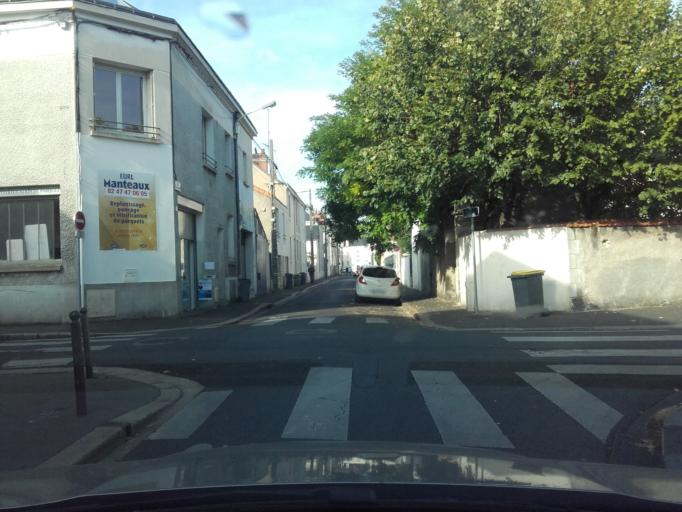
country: FR
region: Centre
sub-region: Departement d'Indre-et-Loire
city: Tours
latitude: 47.3867
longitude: 0.7026
